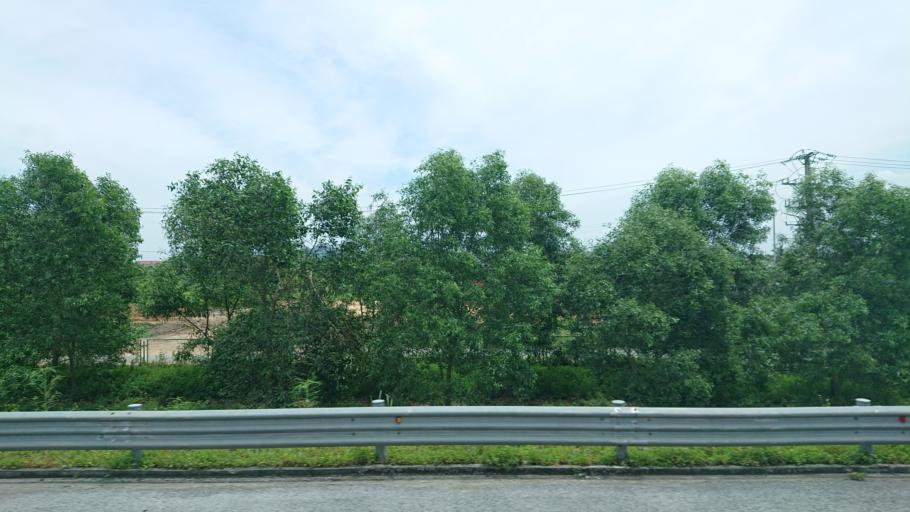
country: VN
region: Hai Phong
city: Nui Doi
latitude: 20.7689
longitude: 106.6313
